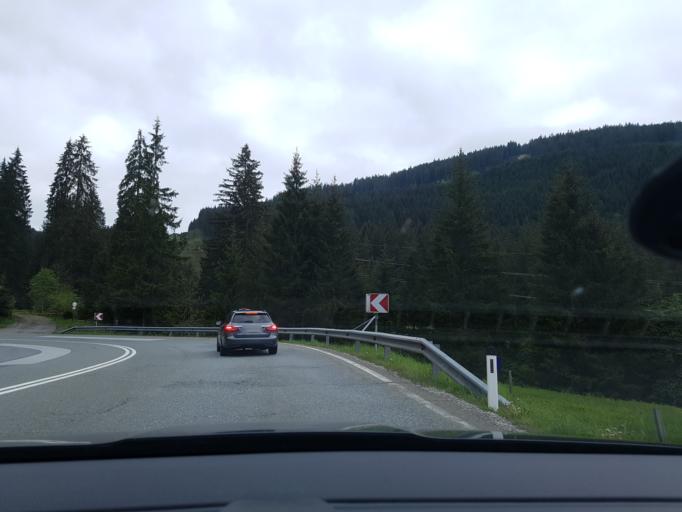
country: AT
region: Tyrol
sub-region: Politischer Bezirk Kitzbuhel
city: Jochberg
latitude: 47.3255
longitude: 12.4067
